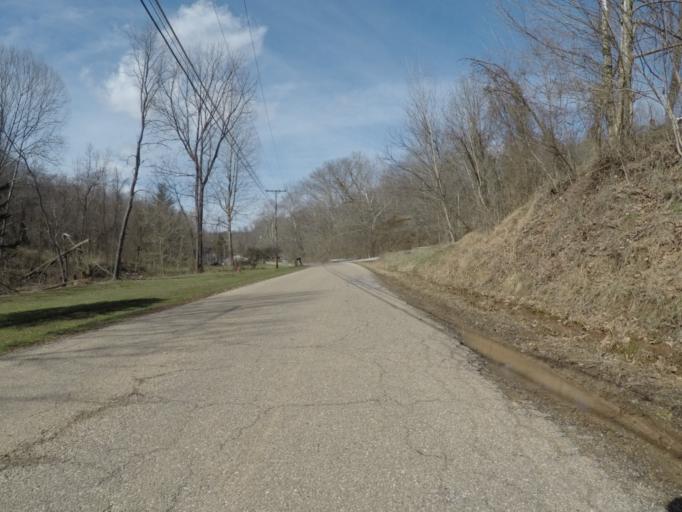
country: US
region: Ohio
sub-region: Lawrence County
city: Burlington
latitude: 38.4802
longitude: -82.5212
